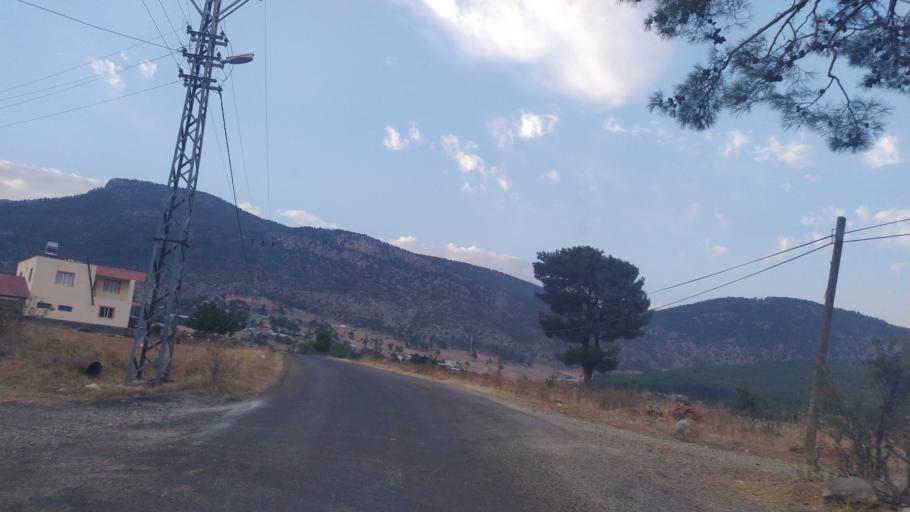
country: TR
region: Mersin
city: Camliyayla
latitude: 37.2345
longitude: 34.7179
